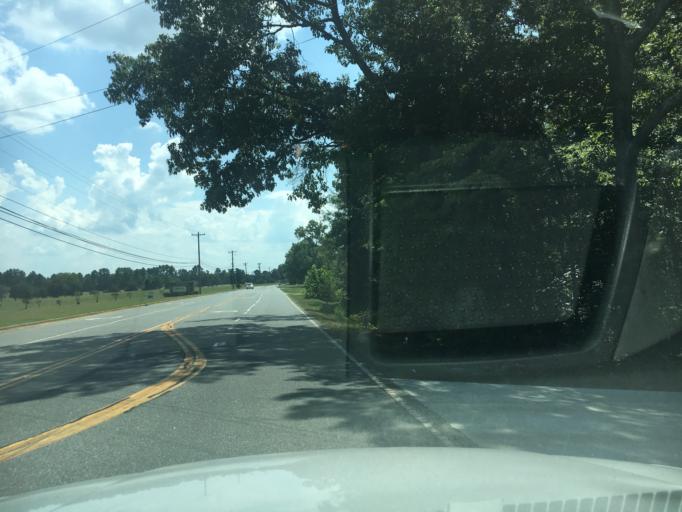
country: US
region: North Carolina
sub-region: Rutherford County
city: Forest City
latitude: 35.2512
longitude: -81.8450
